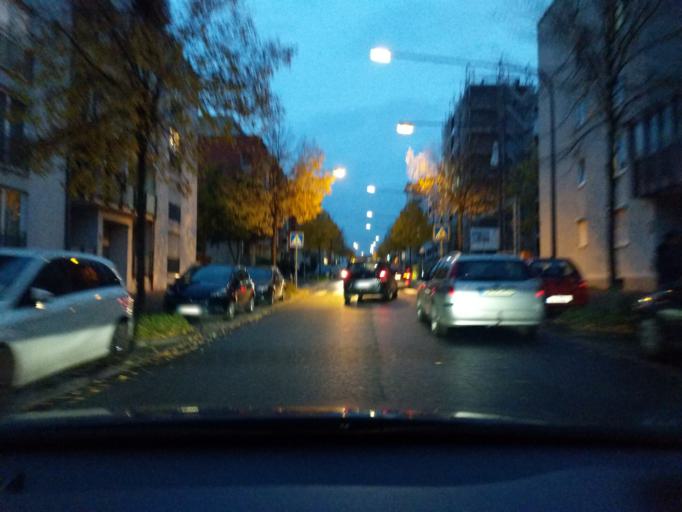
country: DE
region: Hesse
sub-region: Regierungsbezirk Darmstadt
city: Frankfurt am Main
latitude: 50.1561
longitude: 8.6956
